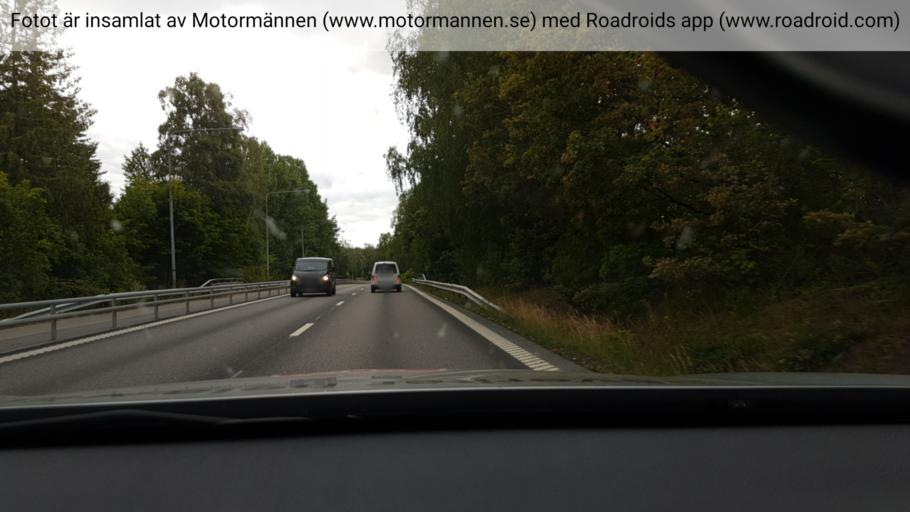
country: SE
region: Stockholm
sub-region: Tyreso Kommun
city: Bollmora
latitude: 59.2208
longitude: 18.2020
